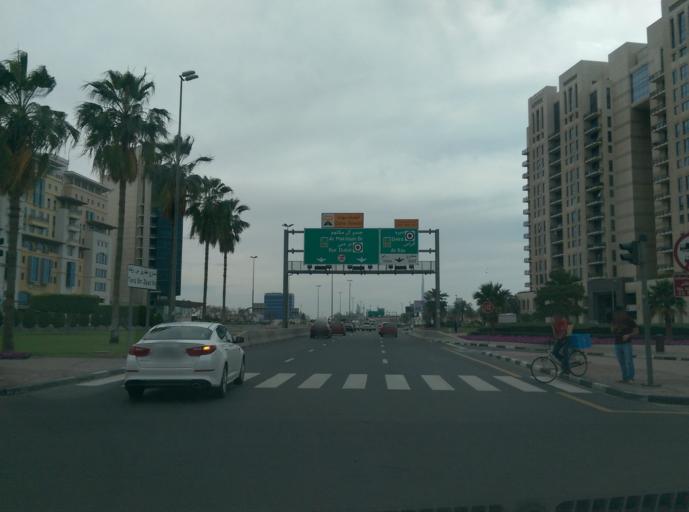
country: AE
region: Ash Shariqah
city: Sharjah
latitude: 25.2586
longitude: 55.3260
